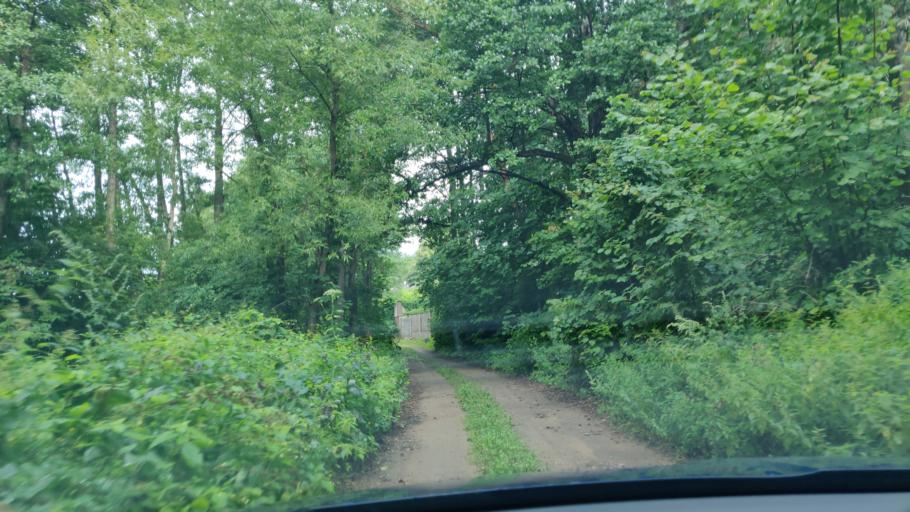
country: LT
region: Vilnius County
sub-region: Trakai
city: Rudiskes
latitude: 54.6091
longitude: 24.8367
